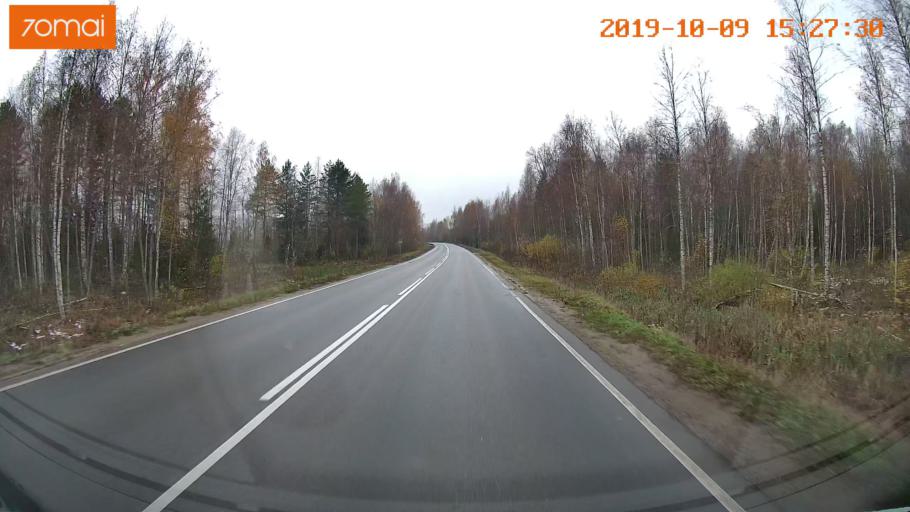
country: RU
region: Kostroma
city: Susanino
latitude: 58.0127
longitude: 41.3780
